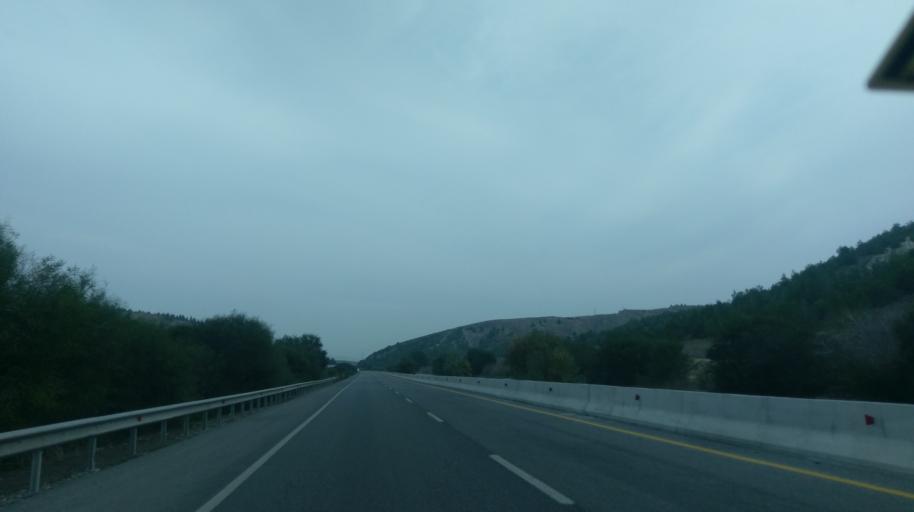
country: CY
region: Lefkosia
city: Akaki
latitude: 35.2064
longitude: 33.1193
